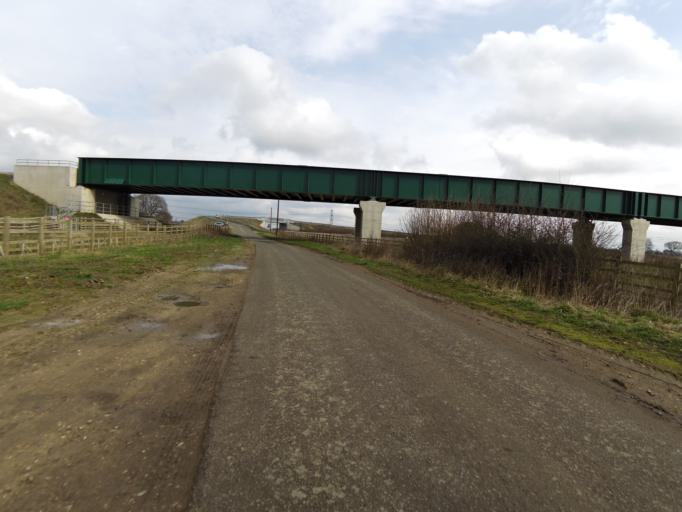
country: GB
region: England
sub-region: Doncaster
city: Moss
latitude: 53.5878
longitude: -1.1239
